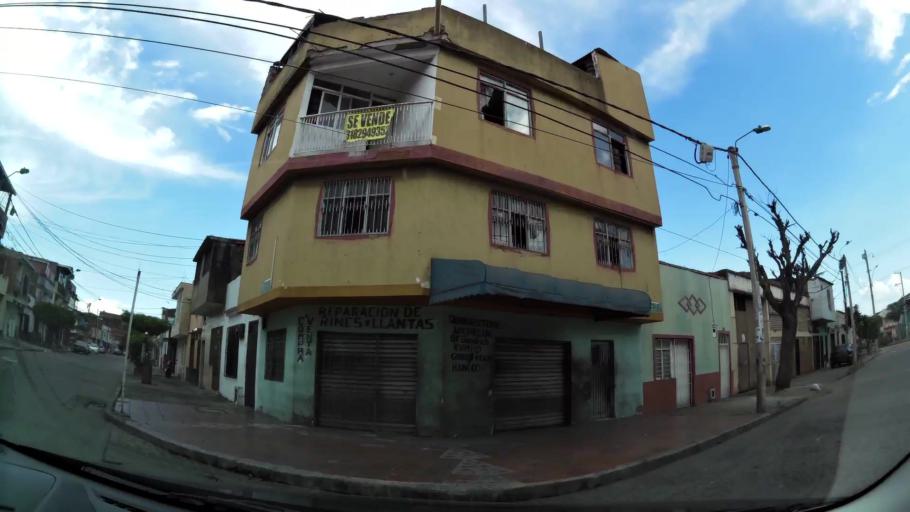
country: CO
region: Valle del Cauca
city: Cali
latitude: 3.4407
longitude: -76.5235
